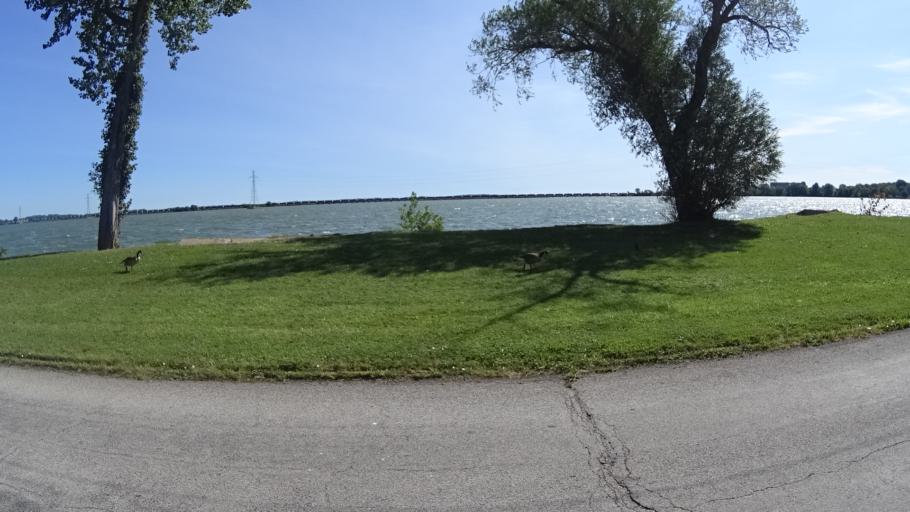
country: US
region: Ohio
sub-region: Erie County
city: Sandusky
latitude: 41.4714
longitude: -82.8240
